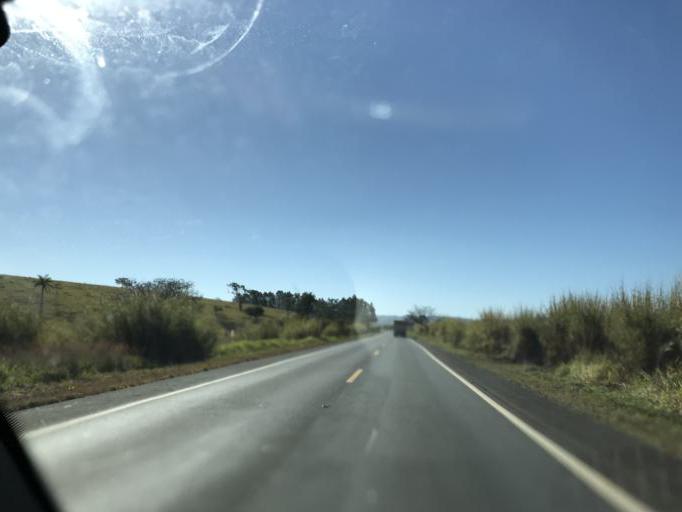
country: BR
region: Minas Gerais
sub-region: Bambui
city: Bambui
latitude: -19.8596
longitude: -45.9863
